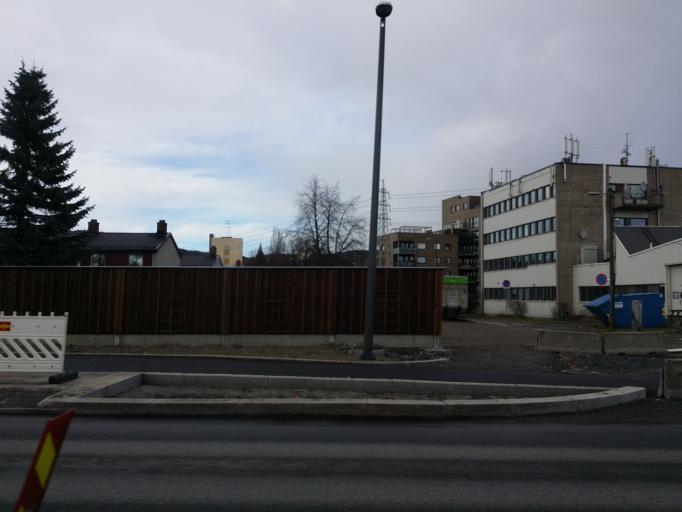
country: NO
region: Oslo
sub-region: Oslo
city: Oslo
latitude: 59.9325
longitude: 10.7987
